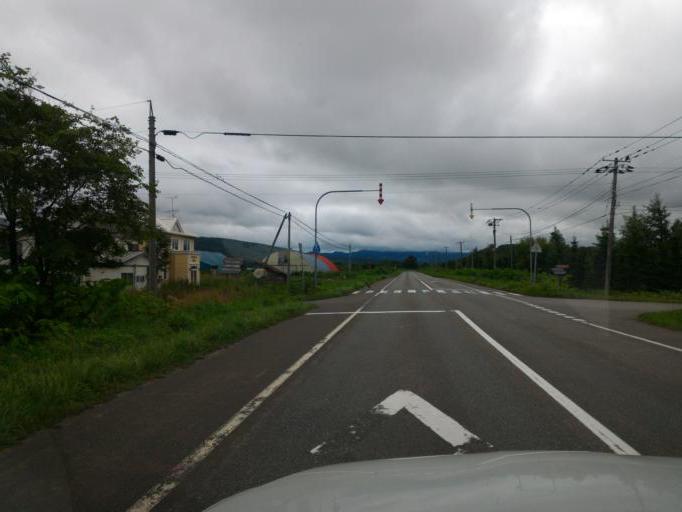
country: JP
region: Hokkaido
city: Makubetsu
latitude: 44.8795
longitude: 142.0234
